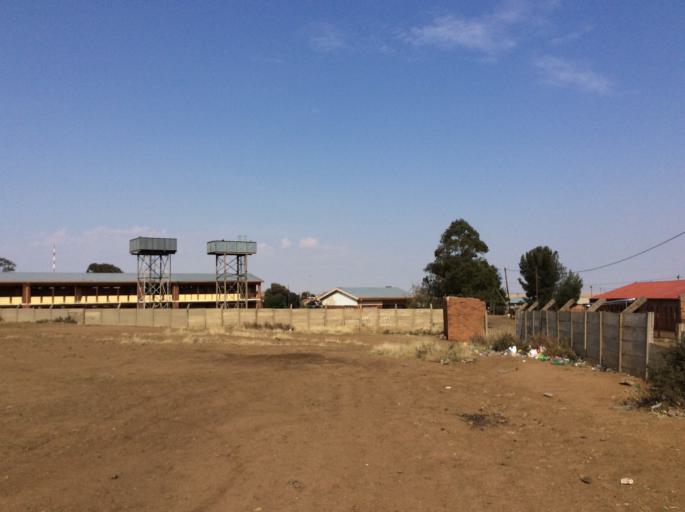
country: LS
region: Mafeteng
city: Mafeteng
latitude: -29.7154
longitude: 27.0311
